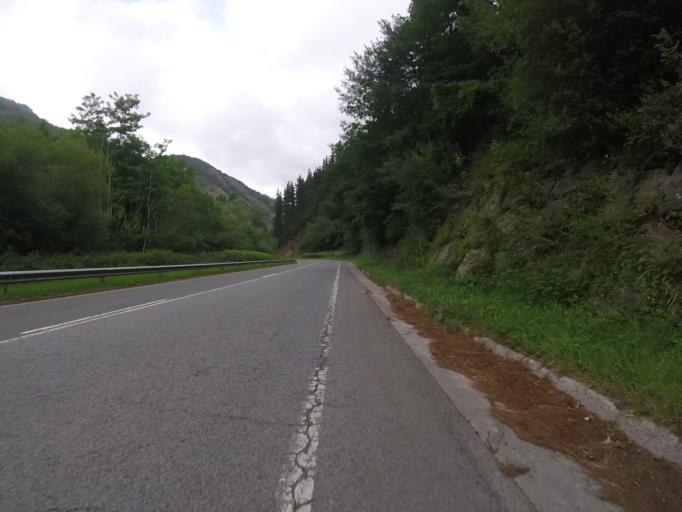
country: ES
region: Navarre
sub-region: Provincia de Navarra
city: Saldias
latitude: 43.1039
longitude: -1.7669
